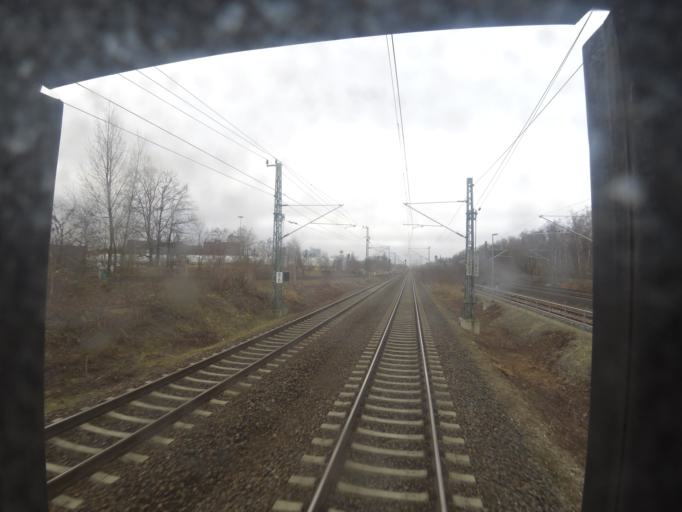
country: DE
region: Berlin
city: Schoneberg Bezirk
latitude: 52.4699
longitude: 13.3631
